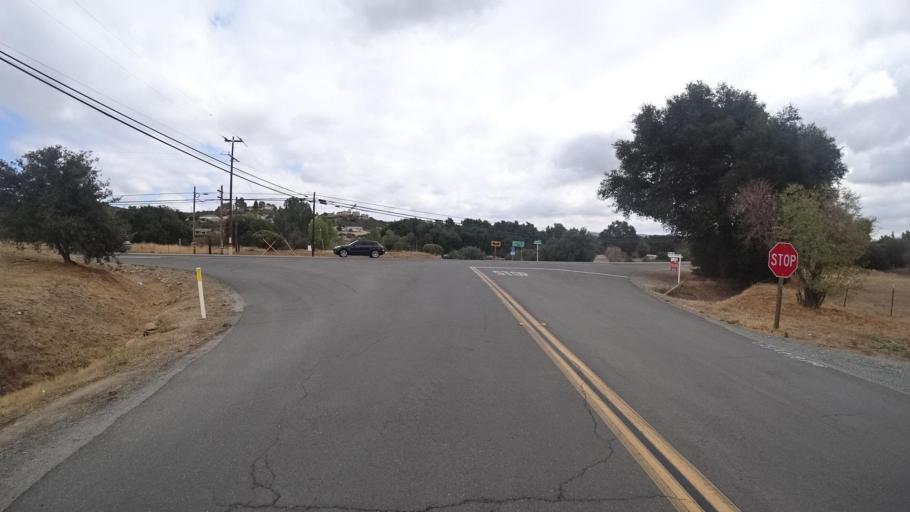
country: US
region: California
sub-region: San Diego County
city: Campo
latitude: 32.6458
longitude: -116.4875
